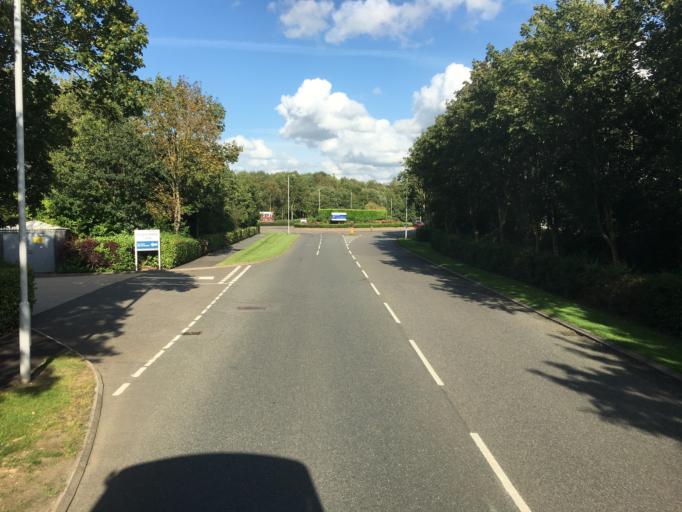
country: GB
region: England
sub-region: Leicestershire
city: Lutterworth
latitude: 52.4556
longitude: -1.2432
